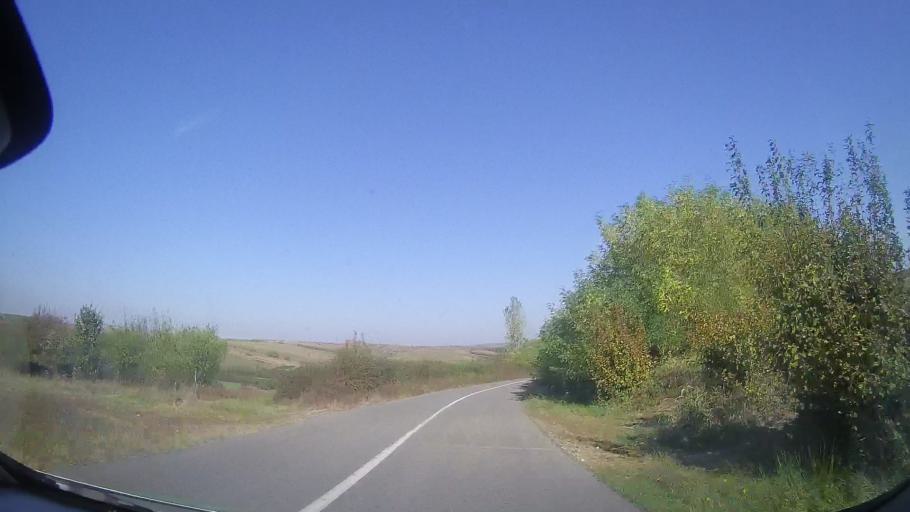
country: RO
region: Timis
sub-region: Comuna Balint
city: Balint
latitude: 45.8325
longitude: 21.8552
